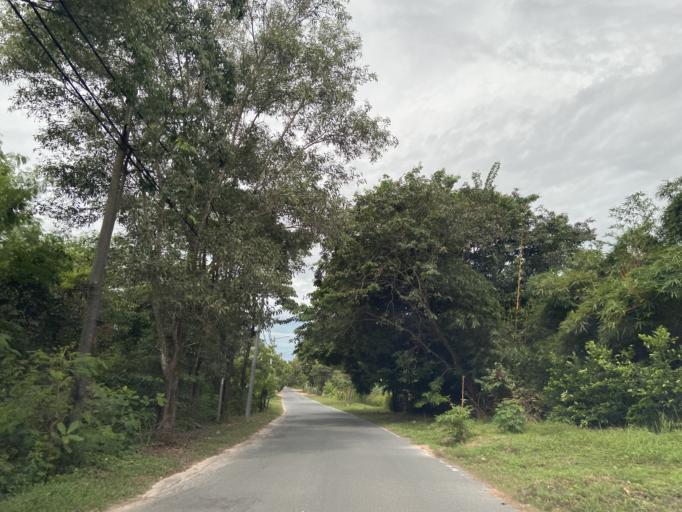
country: SG
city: Singapore
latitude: 1.1049
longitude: 104.0345
